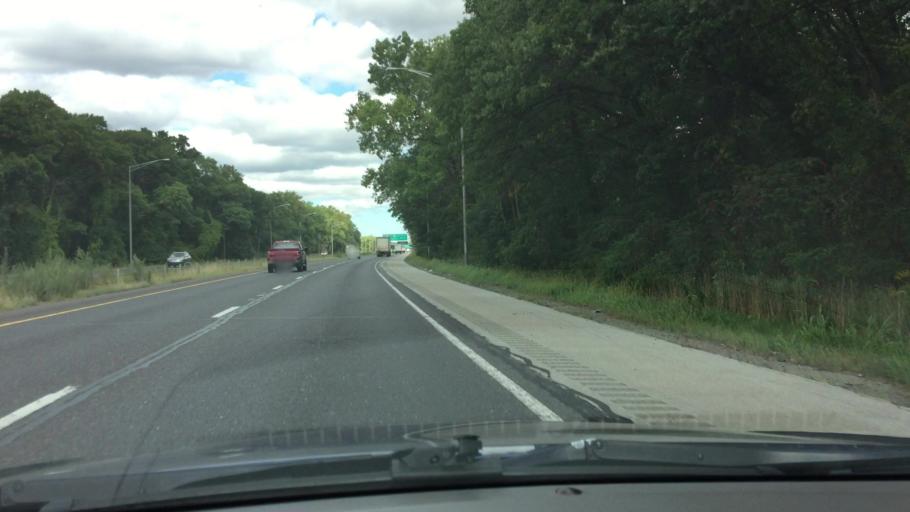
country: US
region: Illinois
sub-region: Cook County
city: Glenwood
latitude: 41.5521
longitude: -87.5834
